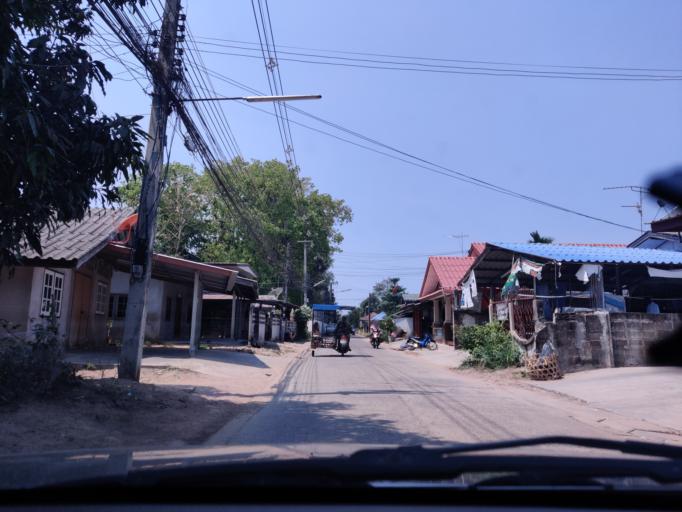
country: TH
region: Sisaket
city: Si Sa Ket
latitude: 15.1044
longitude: 104.3526
